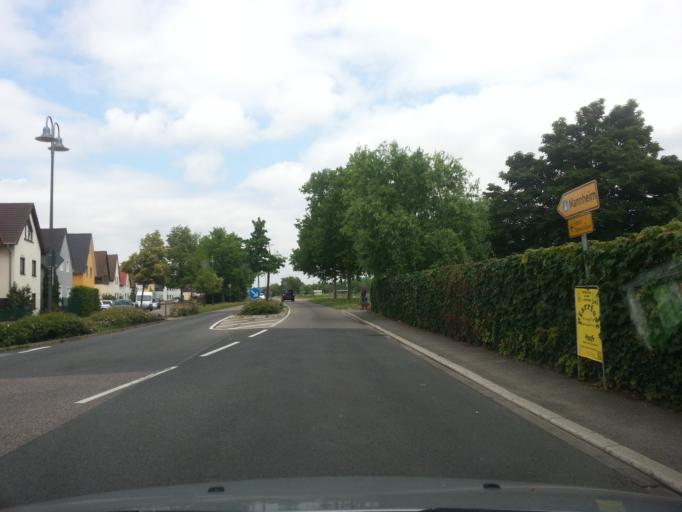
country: DE
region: Baden-Wuerttemberg
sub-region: Karlsruhe Region
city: Bruhl
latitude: 49.4026
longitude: 8.5381
